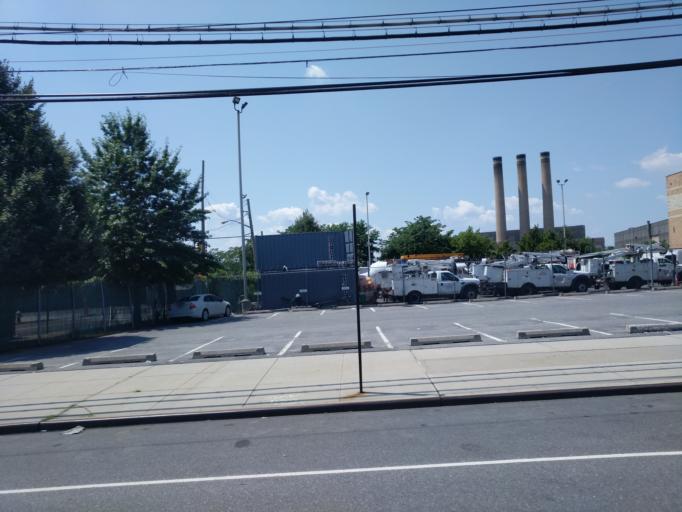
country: US
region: New York
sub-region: Bronx
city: The Bronx
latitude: 40.8248
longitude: -73.8393
